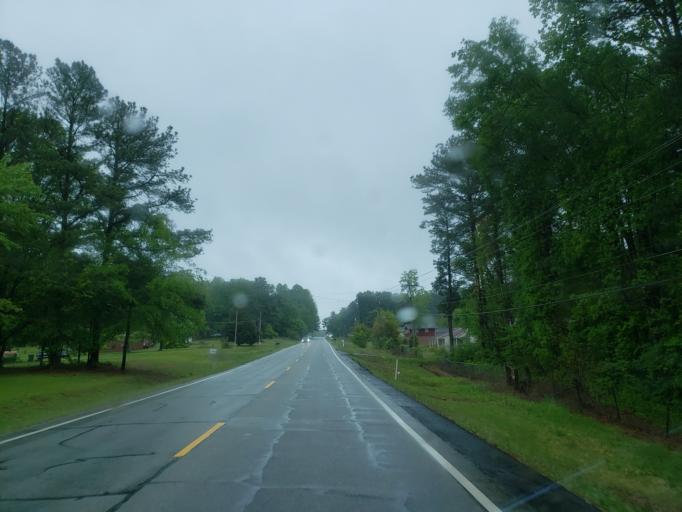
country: US
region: Georgia
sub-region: Paulding County
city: Dallas
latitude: 33.8466
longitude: -84.8593
